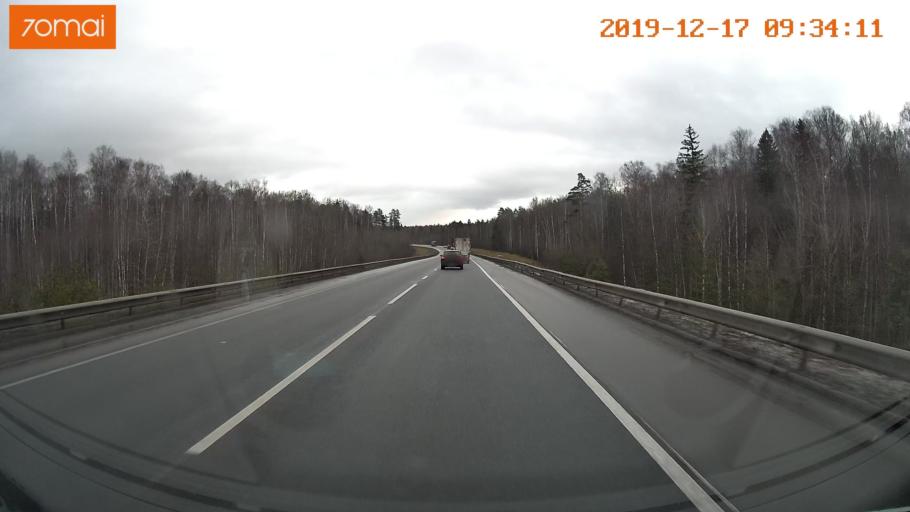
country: RU
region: Vladimir
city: Raduzhnyy
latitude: 56.0739
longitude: 40.2180
